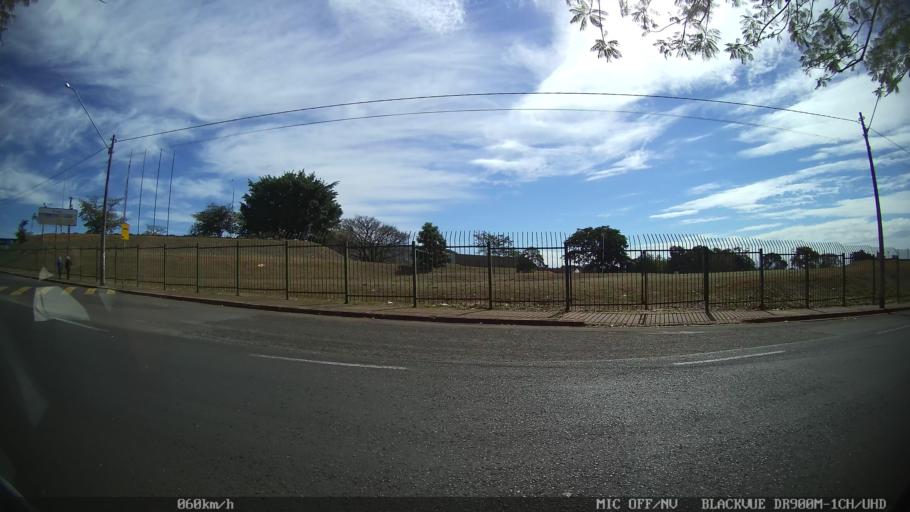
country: BR
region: Sao Paulo
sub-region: Sao Jose Do Rio Preto
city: Sao Jose do Rio Preto
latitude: -20.8330
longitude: -49.3531
